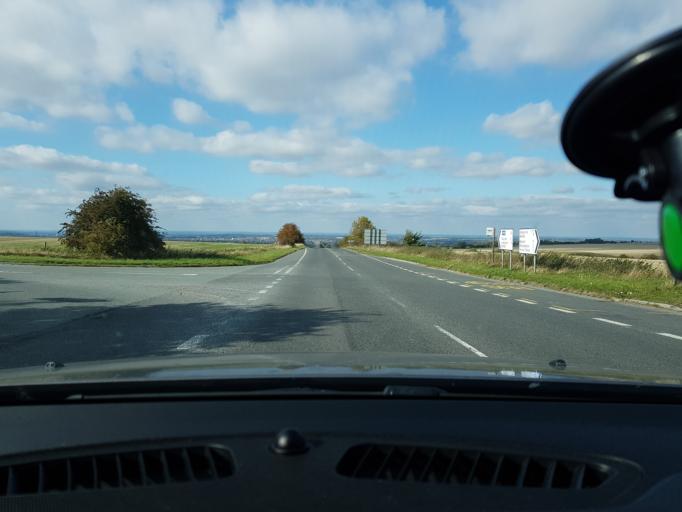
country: GB
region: England
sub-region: Borough of Swindon
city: Wanborough
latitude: 51.5241
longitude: -1.6882
